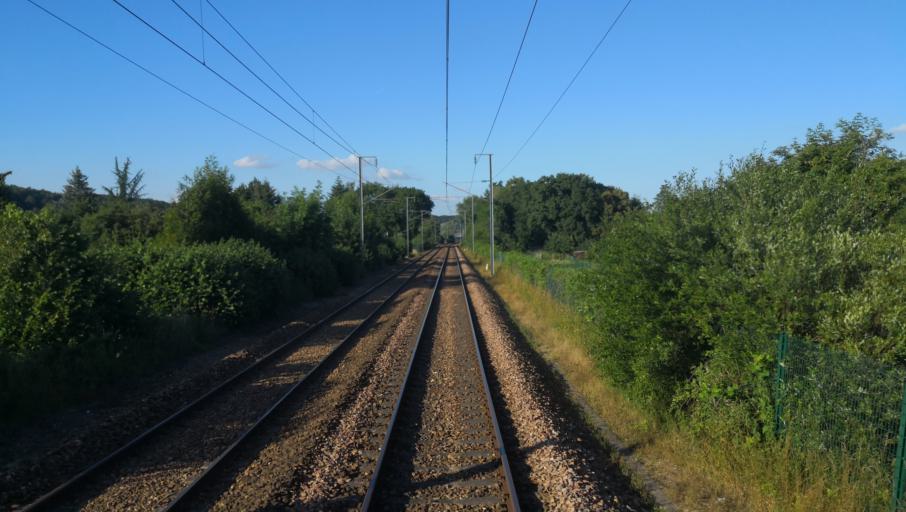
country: FR
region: Haute-Normandie
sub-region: Departement de l'Eure
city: Saint-Sebastien-de-Morsent
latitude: 48.9898
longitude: 1.0382
